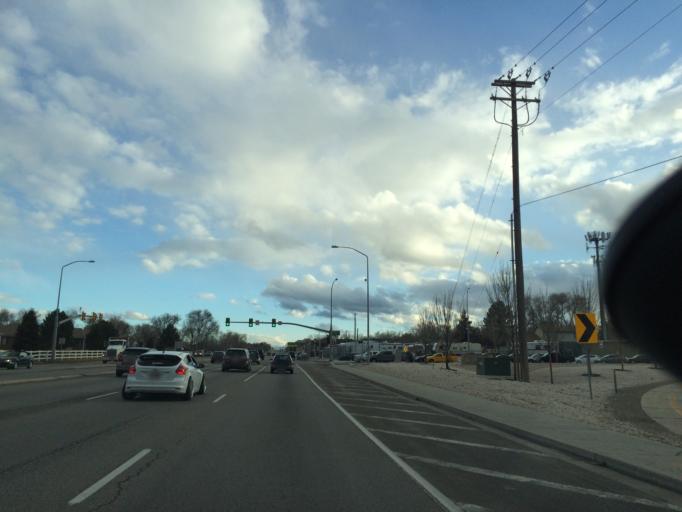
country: US
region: Utah
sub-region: Salt Lake County
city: Taylorsville
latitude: 40.6437
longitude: -111.9389
